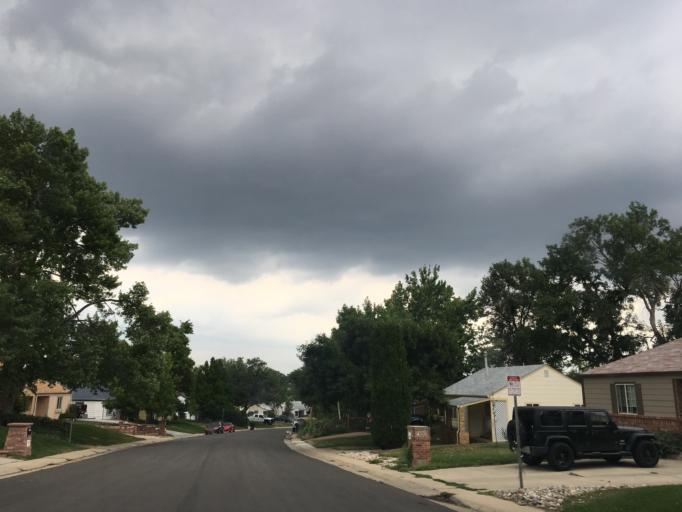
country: US
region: Colorado
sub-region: Arapahoe County
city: Sheridan
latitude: 39.6865
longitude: -105.0140
